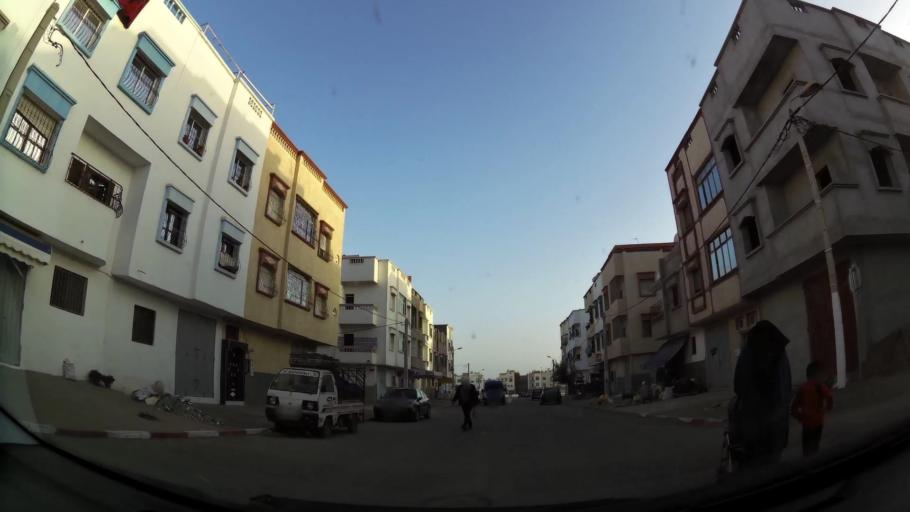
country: MA
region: Oued ed Dahab-Lagouira
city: Dakhla
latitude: 30.3966
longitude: -9.5617
